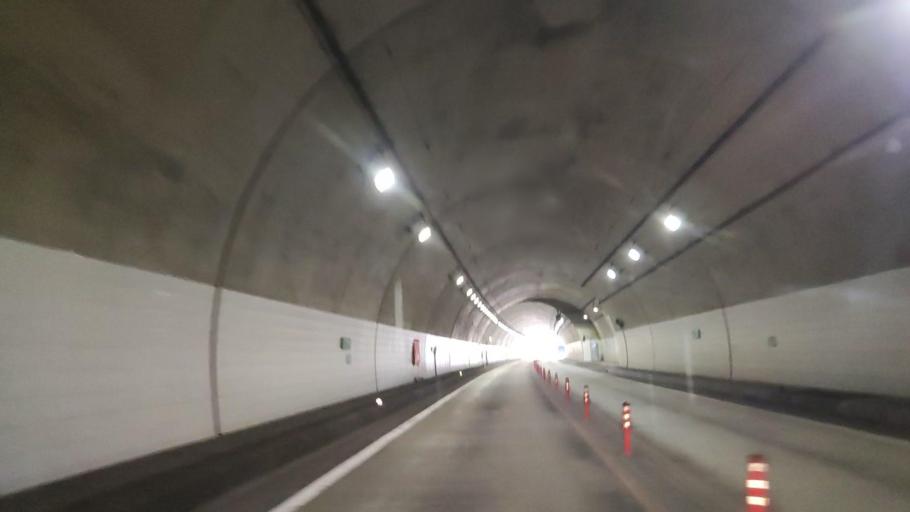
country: JP
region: Akita
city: Odate
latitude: 40.3578
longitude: 140.6917
